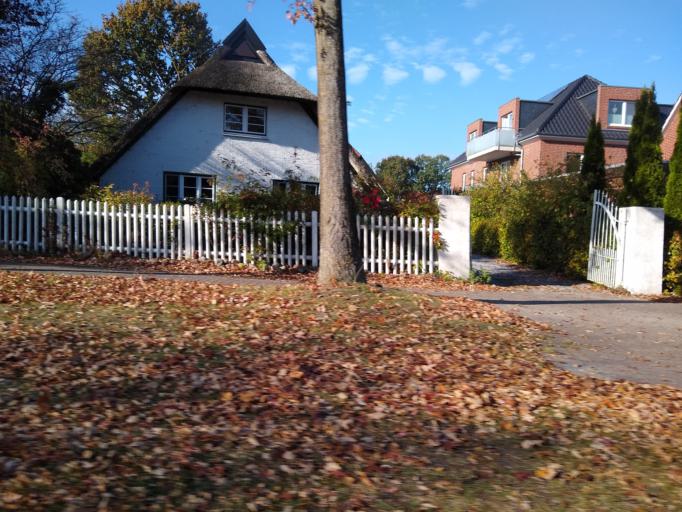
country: DE
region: Lower Saxony
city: Oldenburg
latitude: 53.1799
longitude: 8.2055
